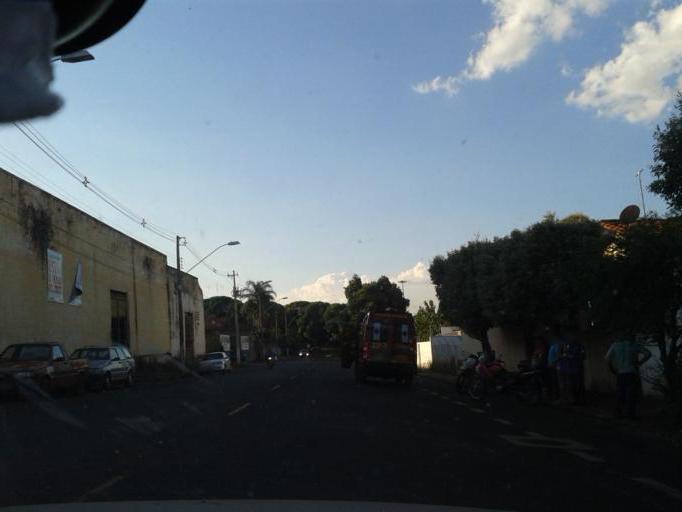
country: BR
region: Minas Gerais
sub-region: Ituiutaba
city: Ituiutaba
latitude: -18.9677
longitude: -49.4608
